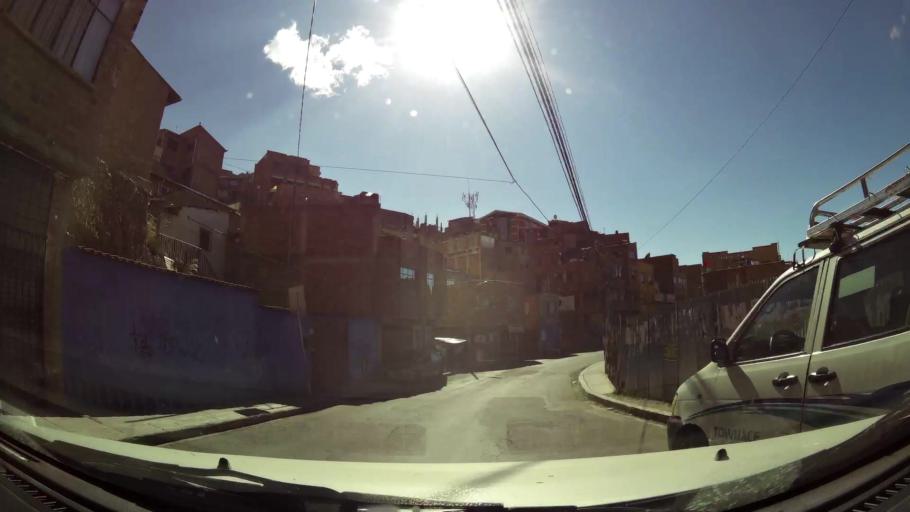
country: BO
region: La Paz
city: La Paz
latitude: -16.5130
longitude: -68.1480
